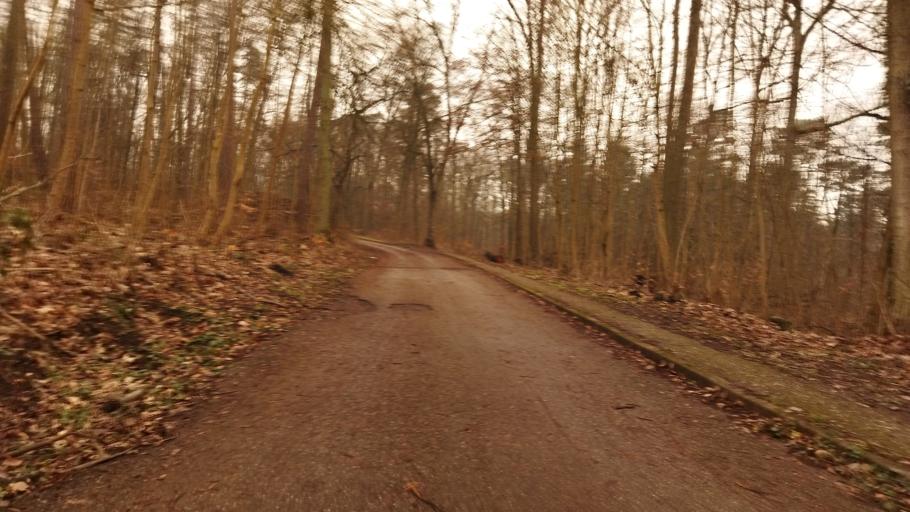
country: DE
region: Baden-Wuerttemberg
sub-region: Regierungsbezirk Stuttgart
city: Weinsberg
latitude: 49.1389
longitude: 9.2788
